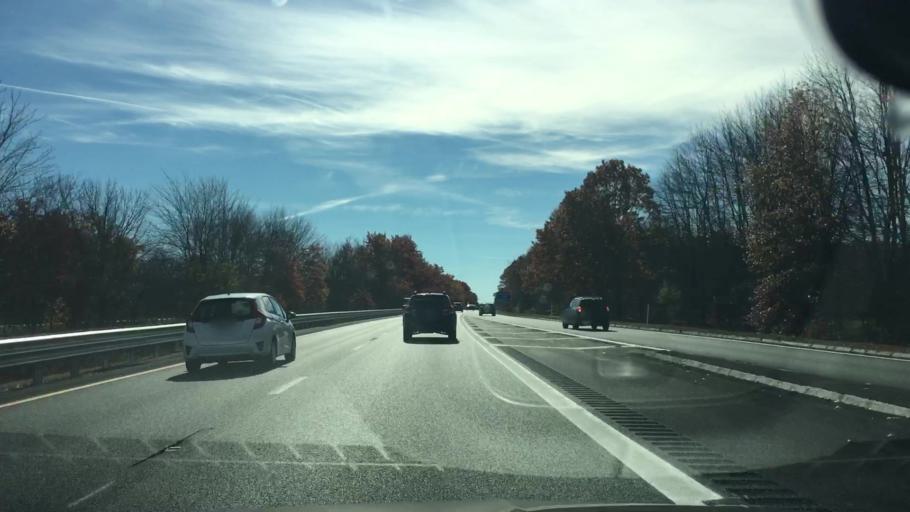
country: US
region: Massachusetts
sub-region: Franklin County
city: South Deerfield
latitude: 42.4638
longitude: -72.6166
